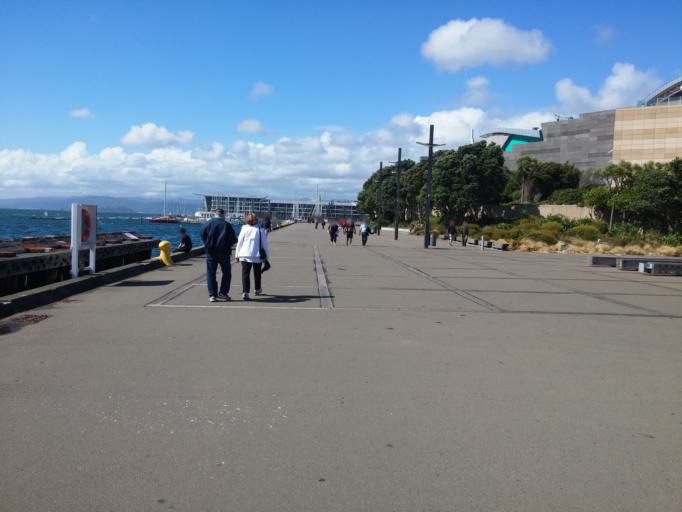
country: NZ
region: Wellington
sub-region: Wellington City
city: Wellington
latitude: -41.2897
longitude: 174.7805
